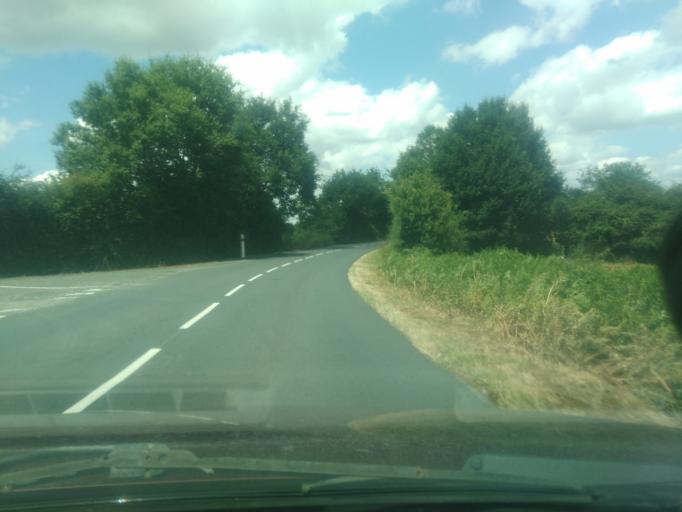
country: FR
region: Pays de la Loire
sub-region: Departement de la Vendee
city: Chauche
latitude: 46.8159
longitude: -1.2666
